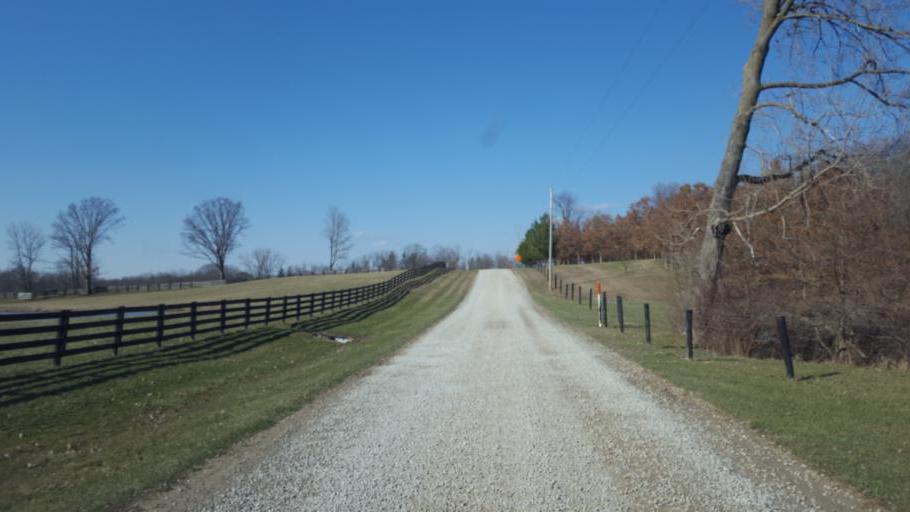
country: US
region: Ohio
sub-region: Morrow County
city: Mount Gilead
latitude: 40.5326
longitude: -82.7780
